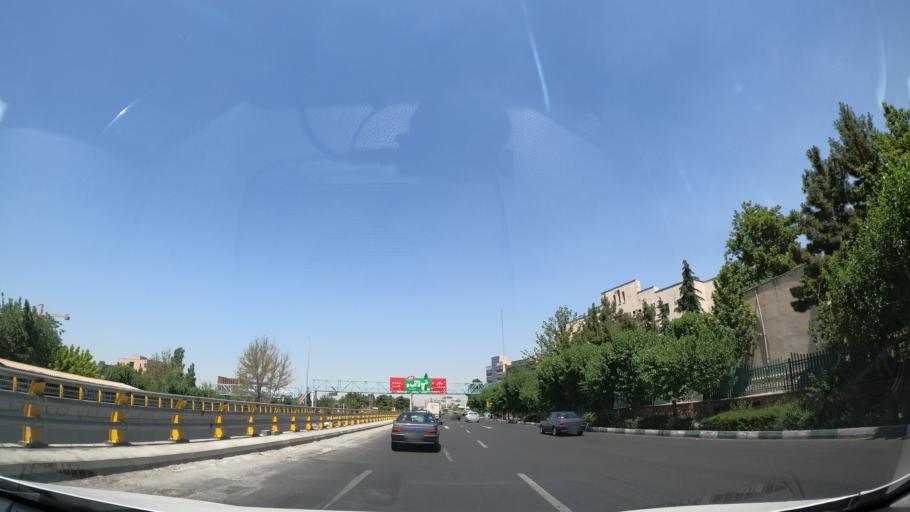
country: IR
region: Tehran
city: Tehran
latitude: 35.7237
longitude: 51.3854
